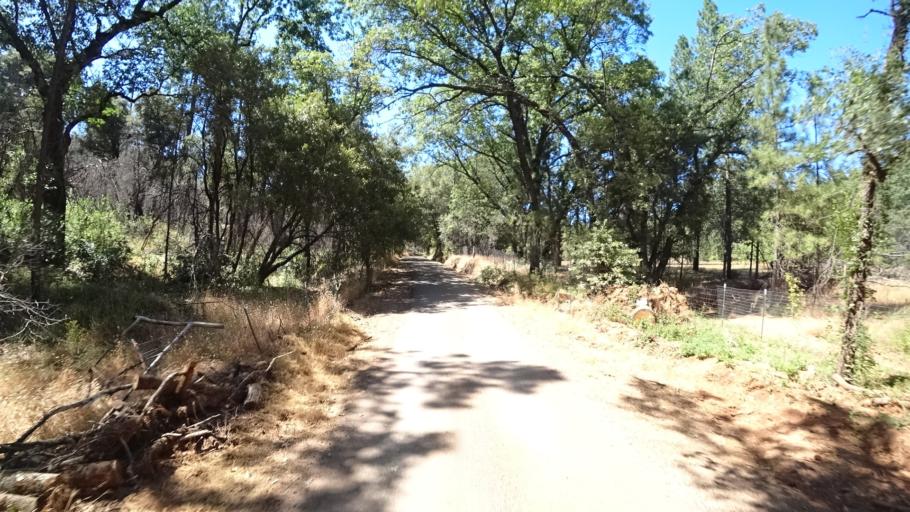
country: US
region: California
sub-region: Calaveras County
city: Mountain Ranch
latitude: 38.2848
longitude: -120.5831
